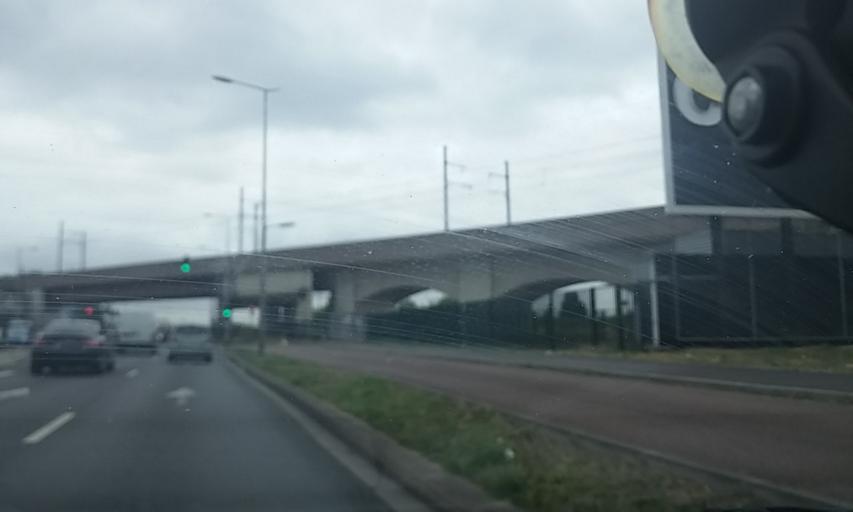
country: FR
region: Ile-de-France
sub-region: Departement du Val-de-Marne
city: Choisy-le-Roi
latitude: 48.7710
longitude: 2.4400
